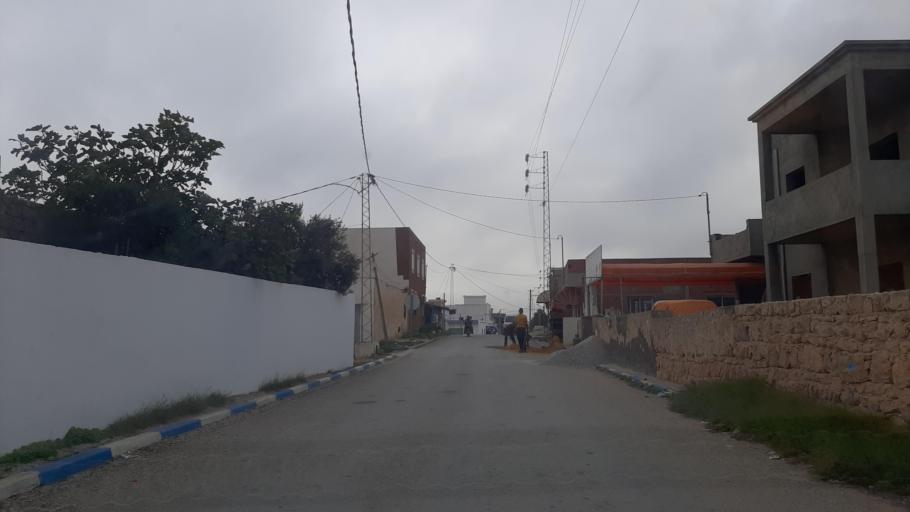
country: TN
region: Nabul
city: Menzel Heurr
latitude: 36.6802
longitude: 10.9253
